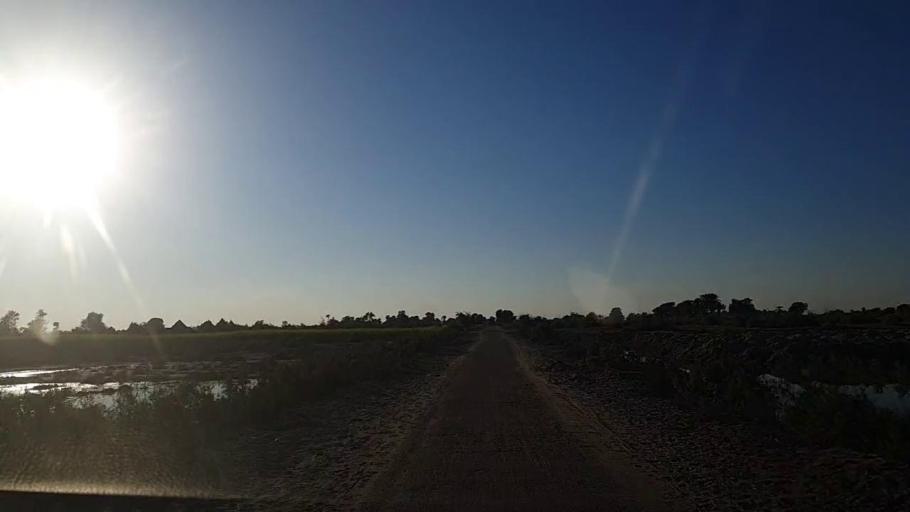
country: PK
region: Sindh
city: Sanghar
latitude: 26.1480
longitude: 68.9237
